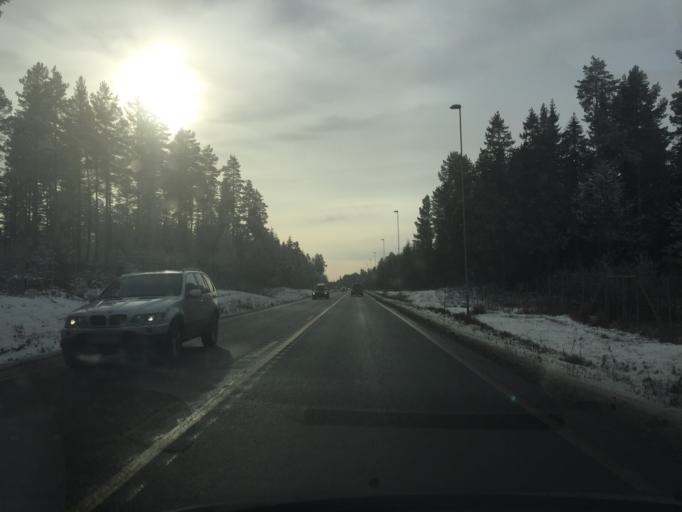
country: NO
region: Hedmark
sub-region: Loten
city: Loten
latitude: 60.7555
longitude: 11.3042
